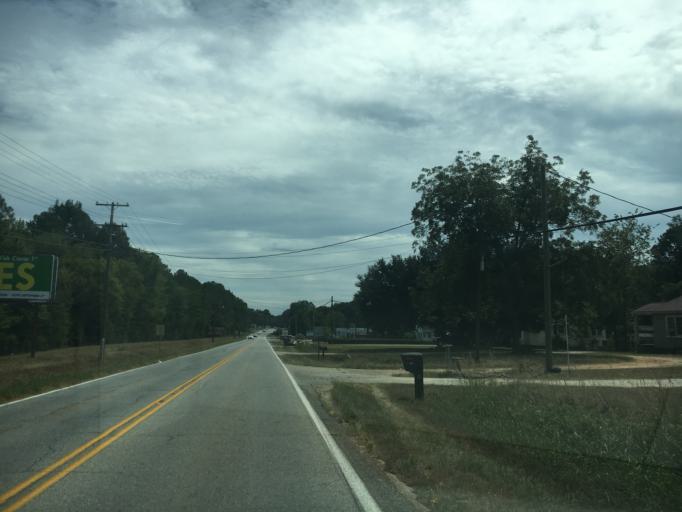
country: US
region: South Carolina
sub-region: Laurens County
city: Laurens
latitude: 34.5179
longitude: -82.0363
